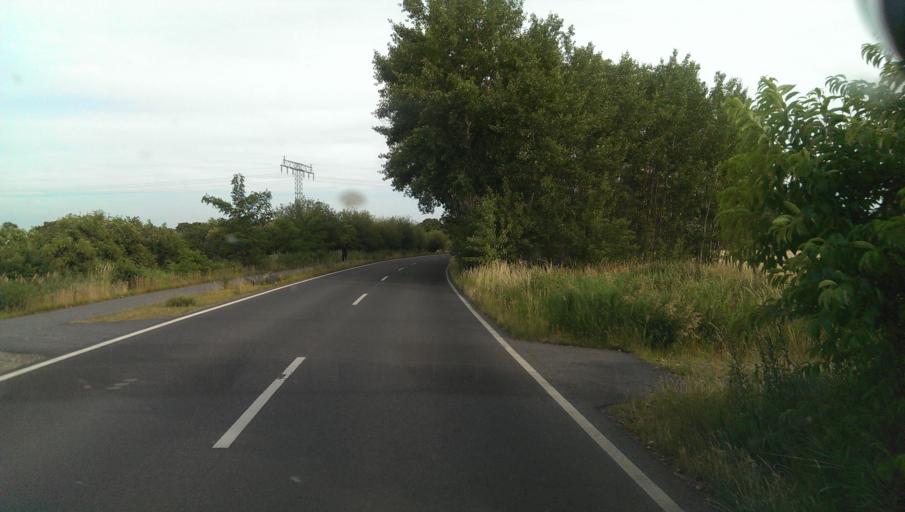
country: DE
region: Brandenburg
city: Grossbeeren
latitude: 52.3473
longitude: 13.2766
